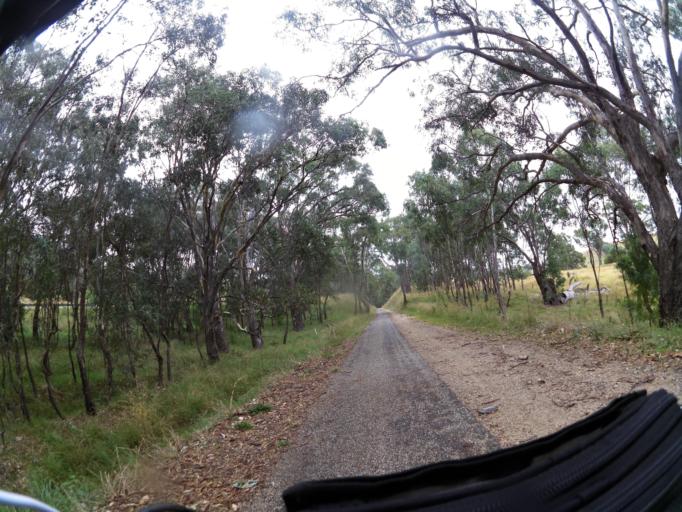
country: AU
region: New South Wales
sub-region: Albury Municipality
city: East Albury
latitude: -36.2240
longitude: 147.1291
